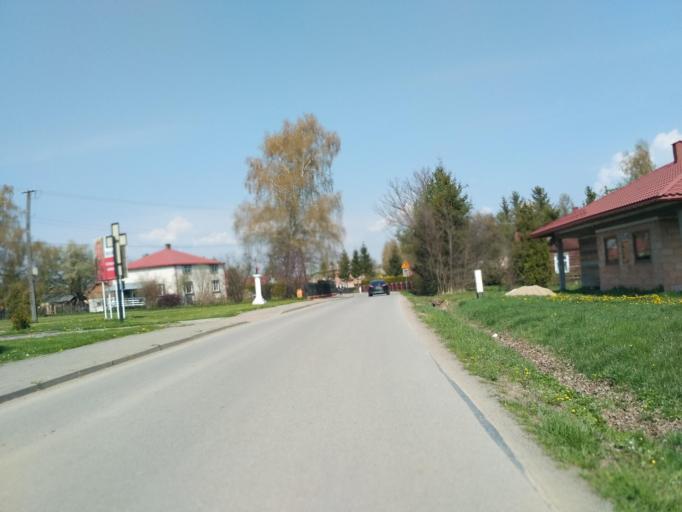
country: PL
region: Subcarpathian Voivodeship
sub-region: Powiat krosnienski
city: Chorkowka
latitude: 49.6291
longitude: 21.7022
